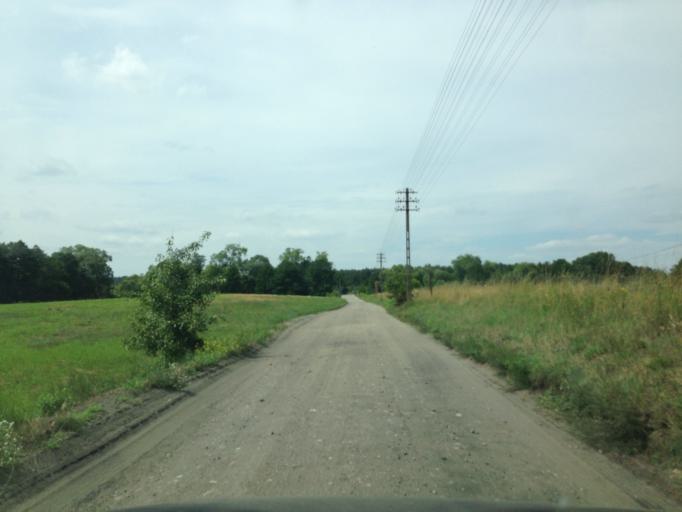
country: PL
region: Kujawsko-Pomorskie
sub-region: Powiat brodnicki
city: Brodnica
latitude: 53.2785
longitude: 19.4819
